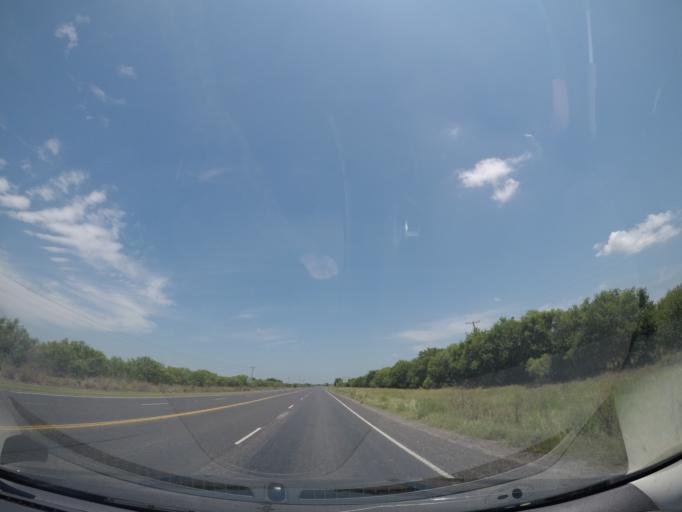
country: US
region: Texas
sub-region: Uvalde County
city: Sabinal
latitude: 29.3166
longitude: -99.4540
